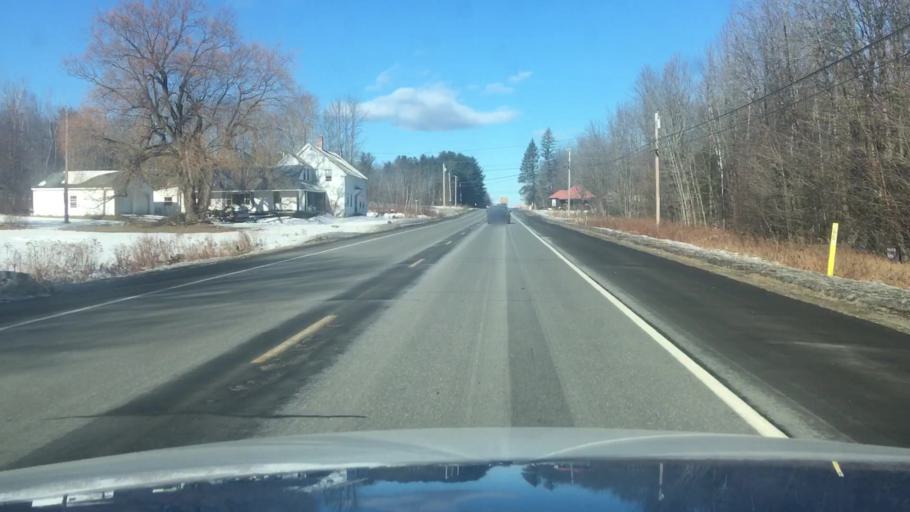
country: US
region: Maine
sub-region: Kennebec County
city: Waterville
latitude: 44.6175
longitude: -69.6696
